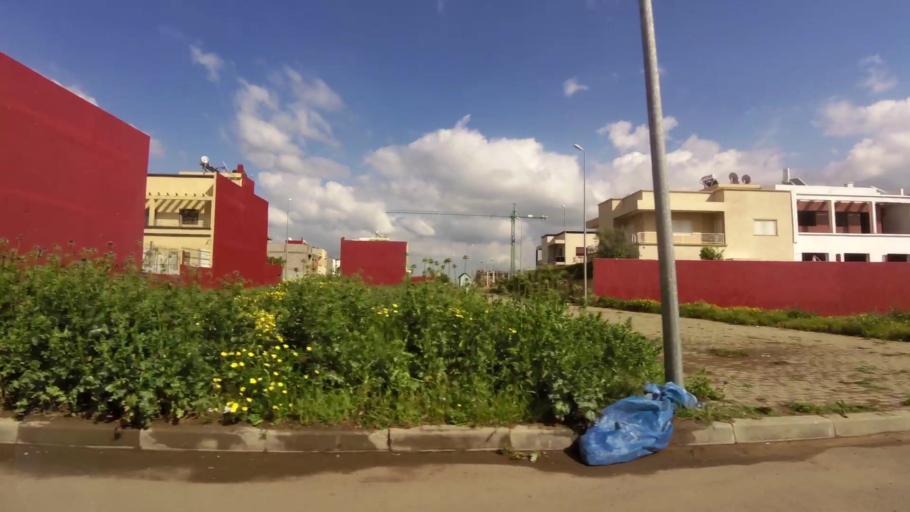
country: MA
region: Chaouia-Ouardigha
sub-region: Settat Province
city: Berrechid
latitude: 33.2574
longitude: -7.5670
